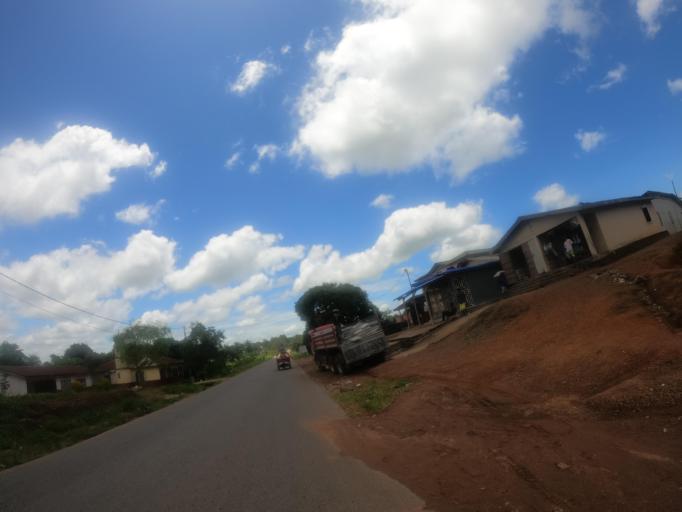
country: SL
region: Northern Province
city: Makeni
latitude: 8.8819
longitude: -12.0786
